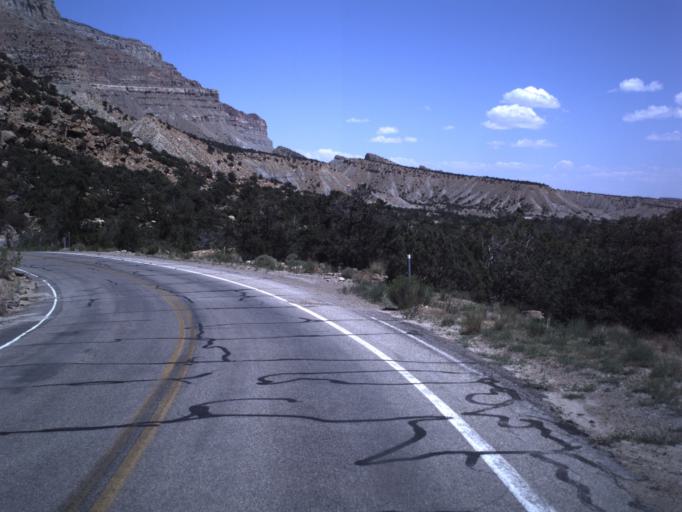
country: US
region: Utah
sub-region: Emery County
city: Orangeville
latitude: 39.2750
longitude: -111.1879
